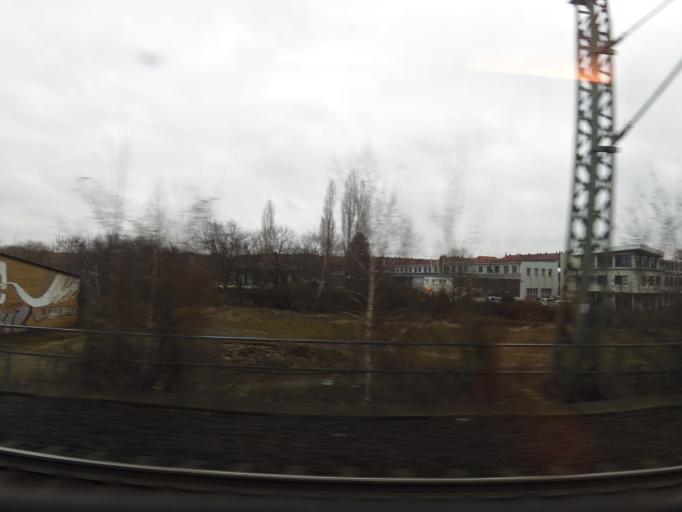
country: DE
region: Lower Saxony
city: Hannover
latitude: 52.3920
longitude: 9.7246
